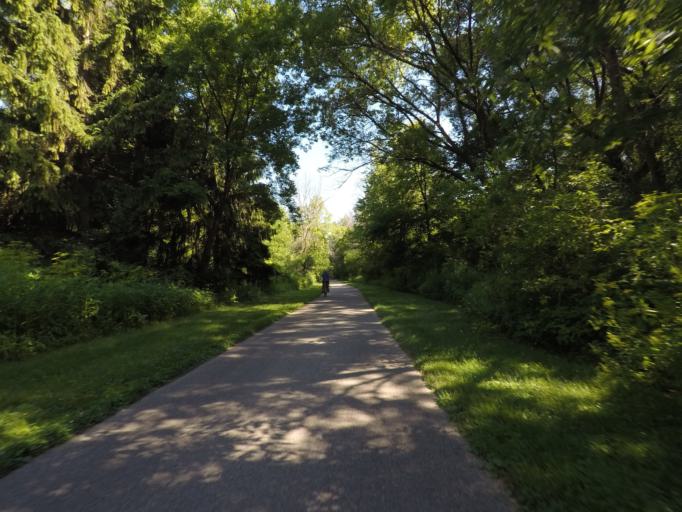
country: US
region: Wisconsin
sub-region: Waukesha County
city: Elm Grove
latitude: 43.0320
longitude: -88.0681
